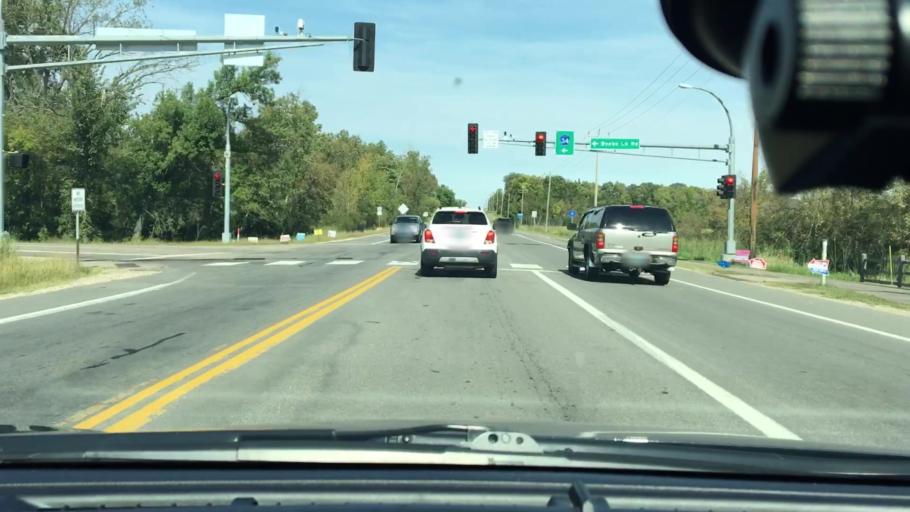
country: US
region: Minnesota
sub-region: Wright County
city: Hanover
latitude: 45.1614
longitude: -93.6660
